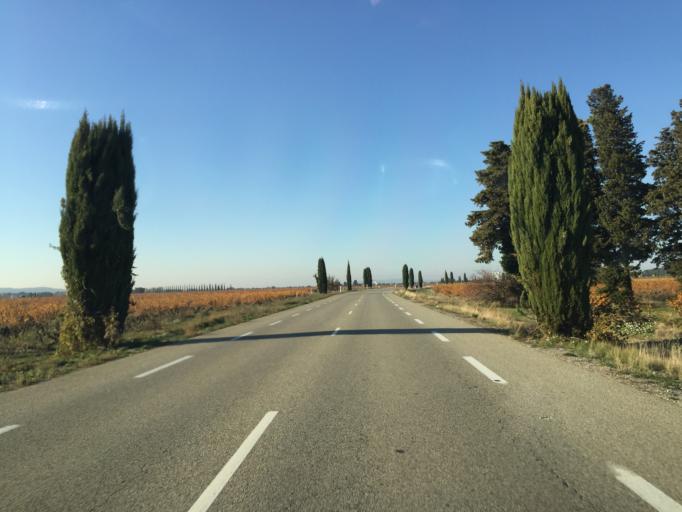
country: FR
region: Provence-Alpes-Cote d'Azur
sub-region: Departement du Vaucluse
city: Sainte-Cecile-les-Vignes
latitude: 44.2317
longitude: 4.9139
